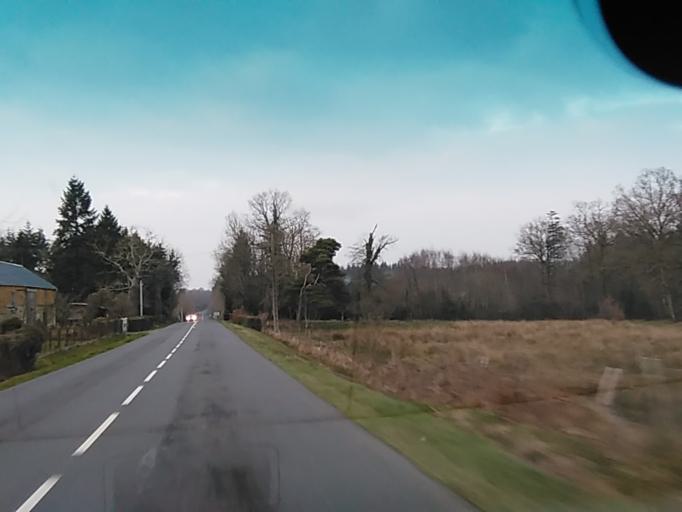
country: FR
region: Lower Normandy
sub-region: Departement de l'Orne
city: Briouze
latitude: 48.6913
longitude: -0.2908
